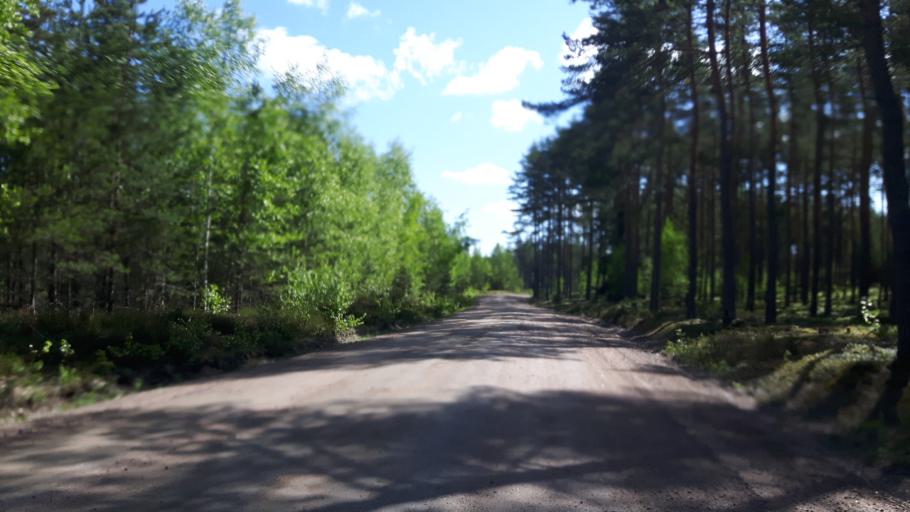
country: FI
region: Kymenlaakso
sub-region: Kotka-Hamina
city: Hamina
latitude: 60.5254
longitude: 27.2654
